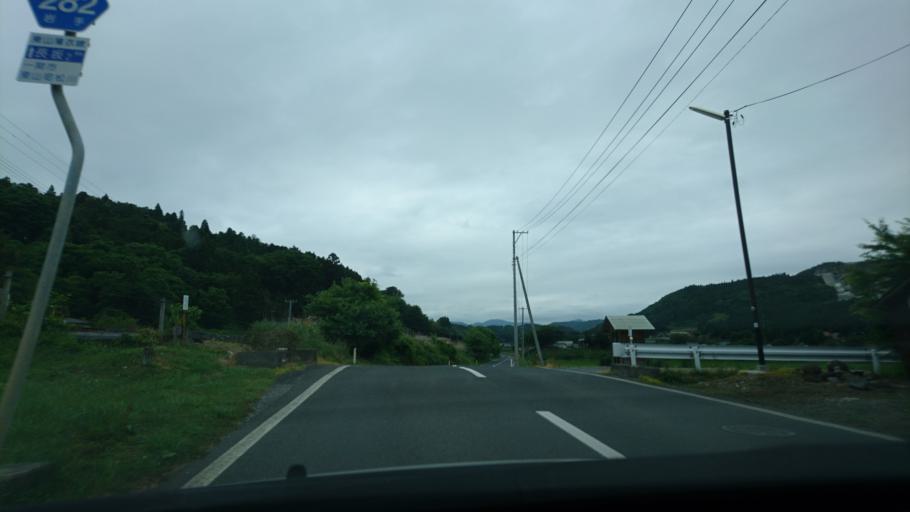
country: JP
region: Iwate
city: Ichinoseki
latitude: 38.9666
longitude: 141.2401
